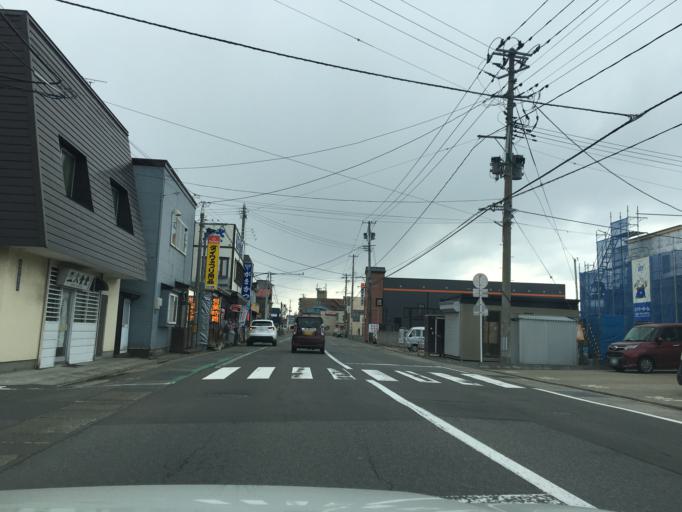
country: JP
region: Aomori
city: Aomori Shi
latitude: 40.8312
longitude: 140.7879
